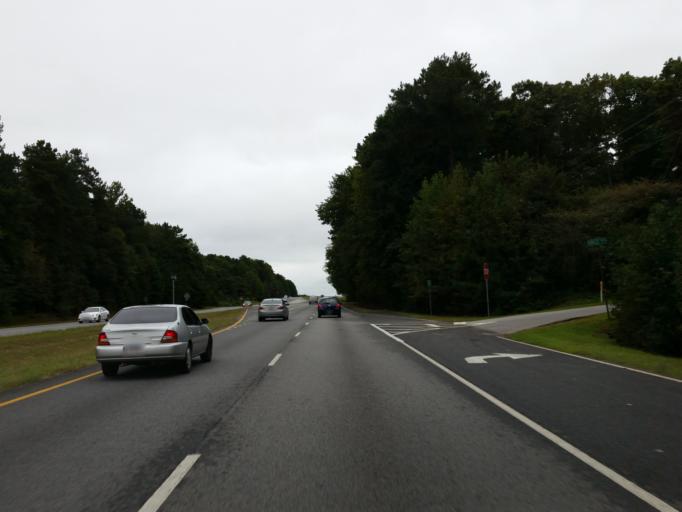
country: US
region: Georgia
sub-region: Clayton County
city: Lovejoy
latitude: 33.4208
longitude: -84.3178
